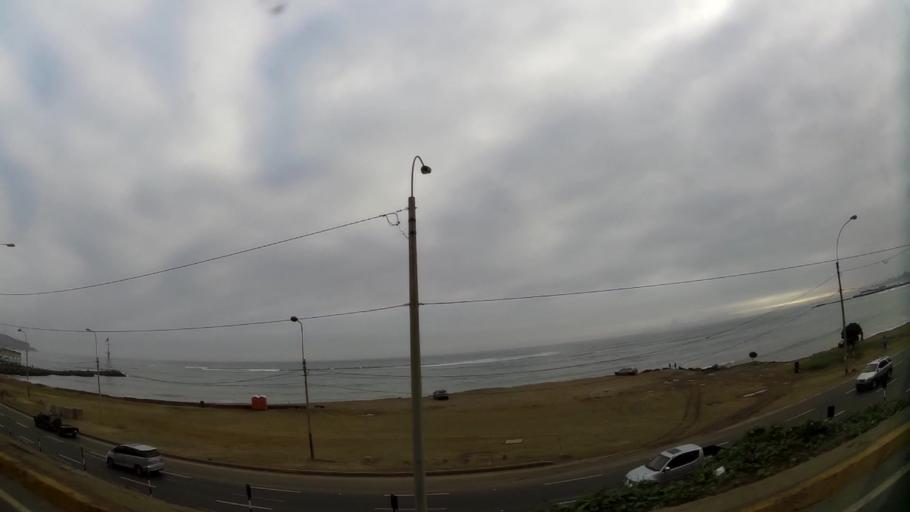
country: PE
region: Lima
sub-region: Lima
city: Surco
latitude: -12.1377
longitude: -77.0282
